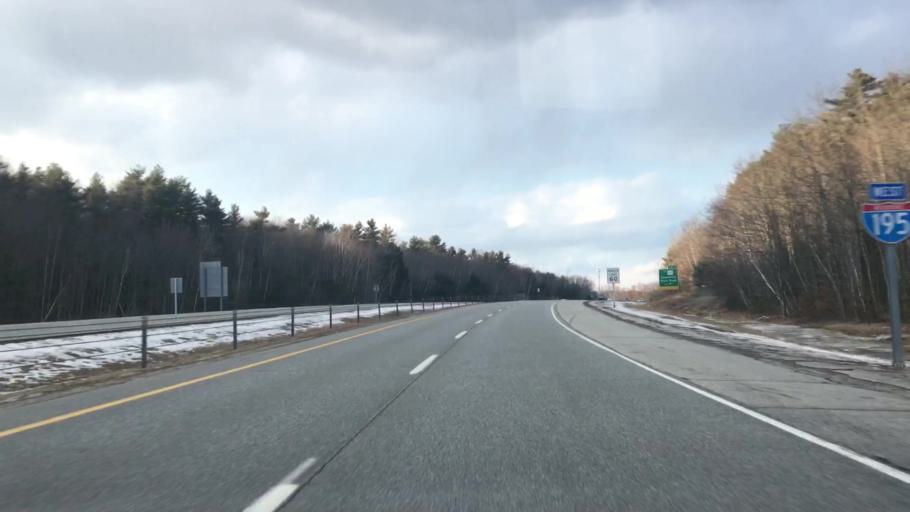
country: US
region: Maine
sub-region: York County
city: Saco
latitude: 43.5151
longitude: -70.4389
